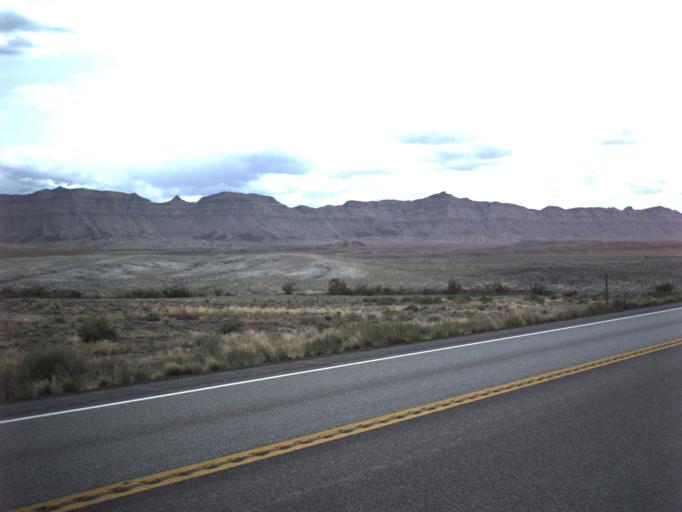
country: US
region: Utah
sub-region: Carbon County
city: East Carbon City
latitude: 39.3675
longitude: -110.3947
